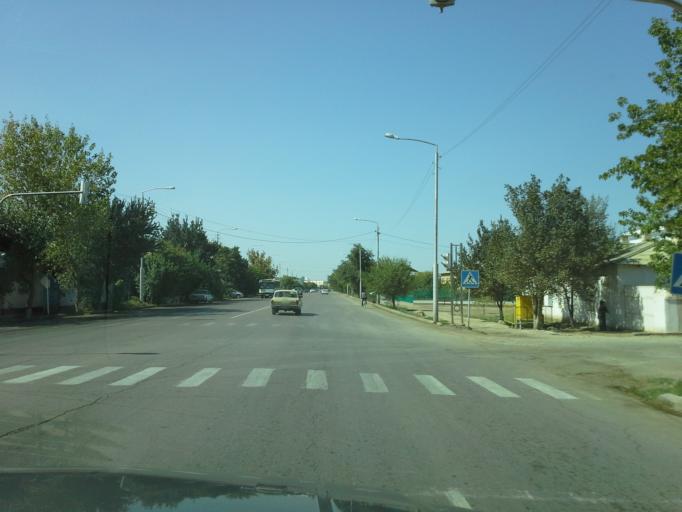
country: TM
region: Dasoguz
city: Dasoguz
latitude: 41.8182
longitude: 59.9835
